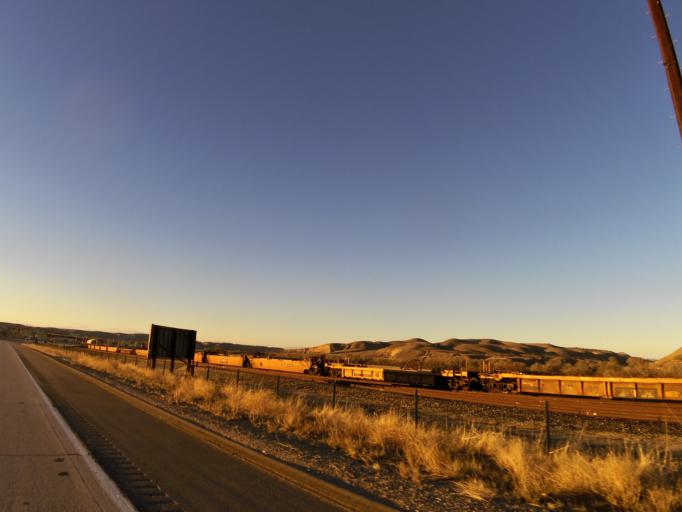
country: US
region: California
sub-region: San Luis Obispo County
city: San Miguel
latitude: 35.7802
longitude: -120.7213
